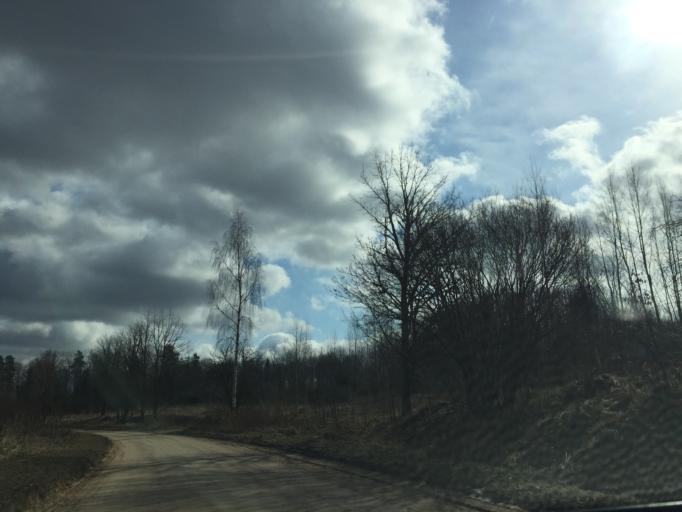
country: LV
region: Vecumnieki
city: Vecumnieki
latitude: 56.5840
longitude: 24.5656
